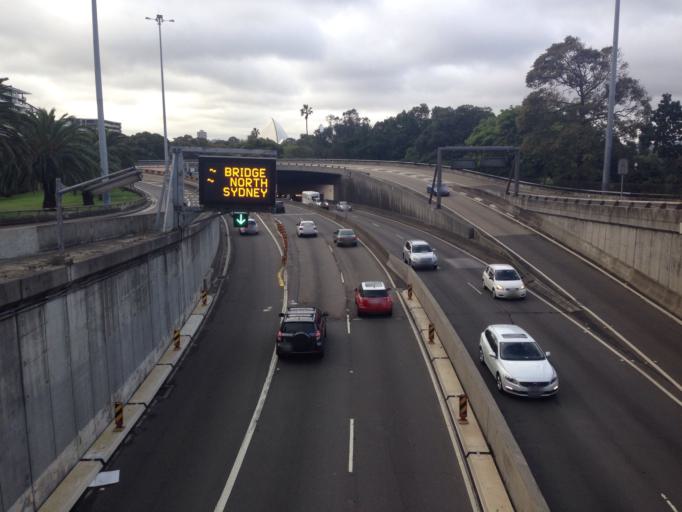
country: AU
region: New South Wales
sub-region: City of Sydney
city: Sydney
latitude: -33.8630
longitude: 151.2134
